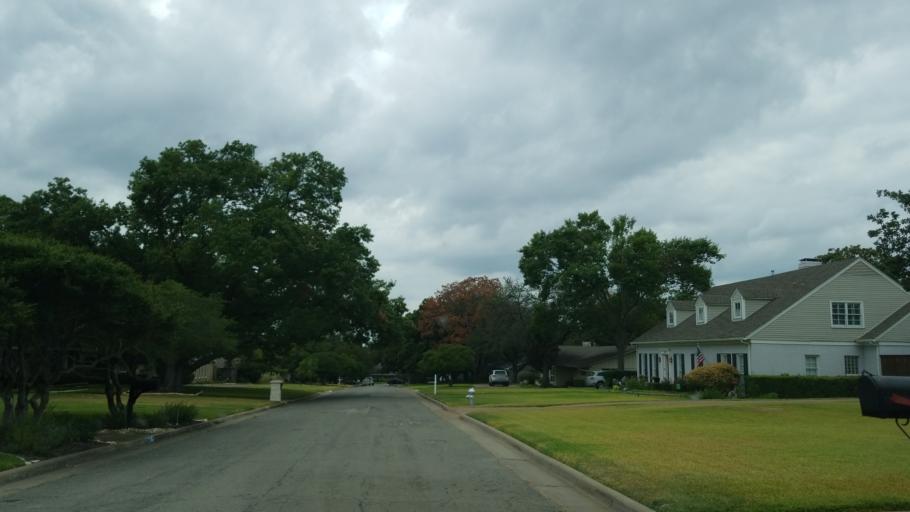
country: US
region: Texas
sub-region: Dallas County
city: Richardson
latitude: 32.9421
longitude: -96.7756
